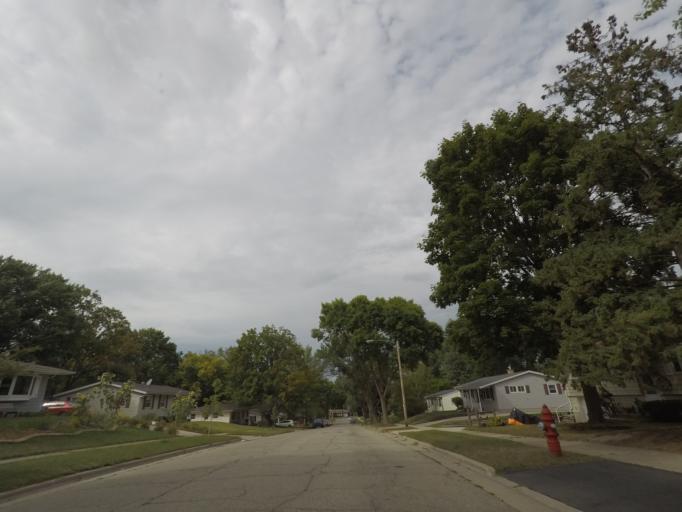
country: US
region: Wisconsin
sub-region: Dane County
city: Monona
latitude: 43.0748
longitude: -89.3020
